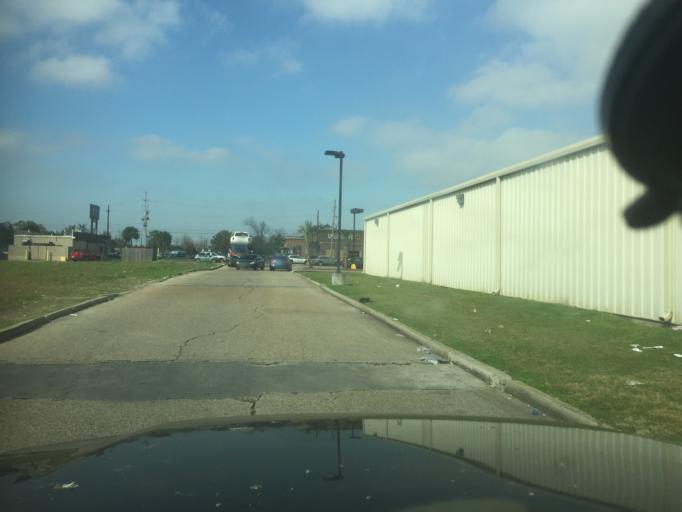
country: US
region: Louisiana
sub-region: Saint Bernard Parish
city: Arabi
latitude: 30.0036
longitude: -90.0376
